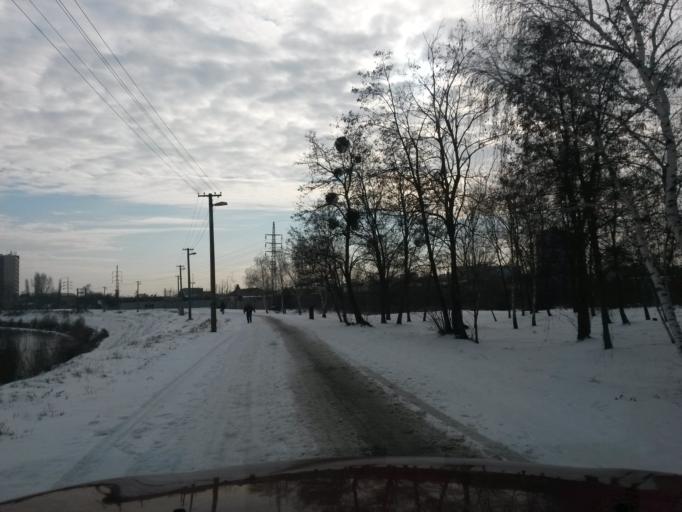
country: SK
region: Kosicky
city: Kosice
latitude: 48.7265
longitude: 21.2702
